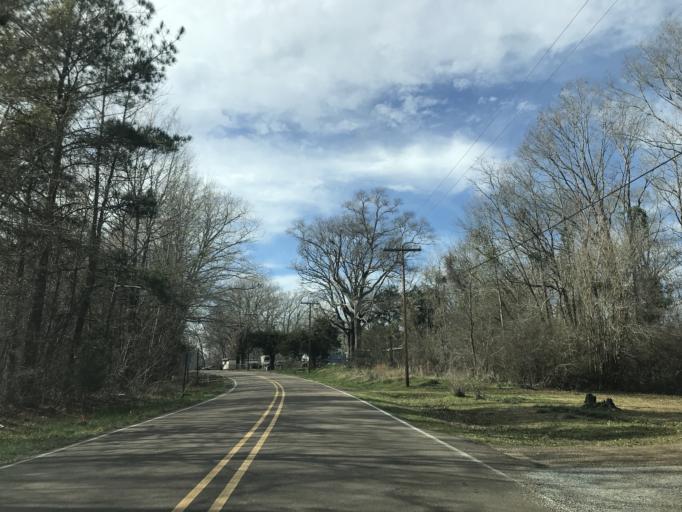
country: US
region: Mississippi
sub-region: Hinds County
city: Edwards
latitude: 32.1110
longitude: -90.6018
